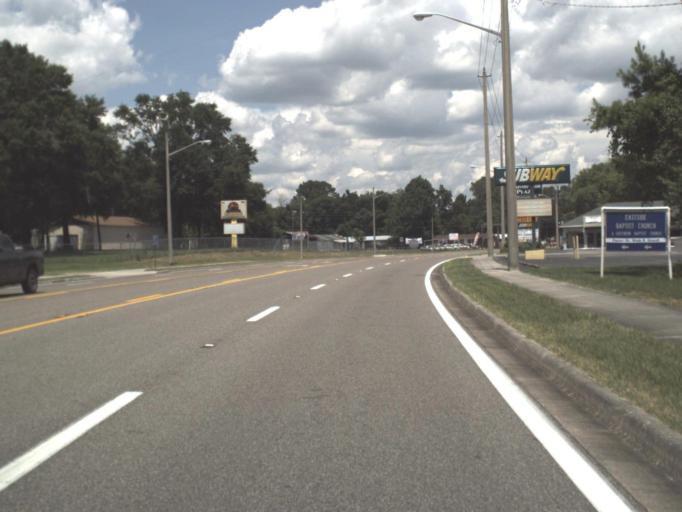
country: US
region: Florida
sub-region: Columbia County
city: Watertown
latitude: 30.1831
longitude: -82.6120
